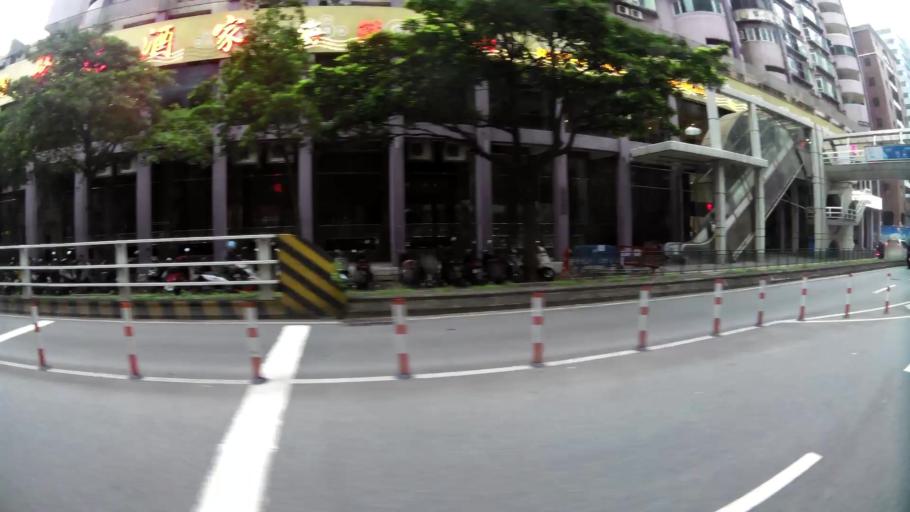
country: MO
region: Macau
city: Macau
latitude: 22.1914
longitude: 113.5456
